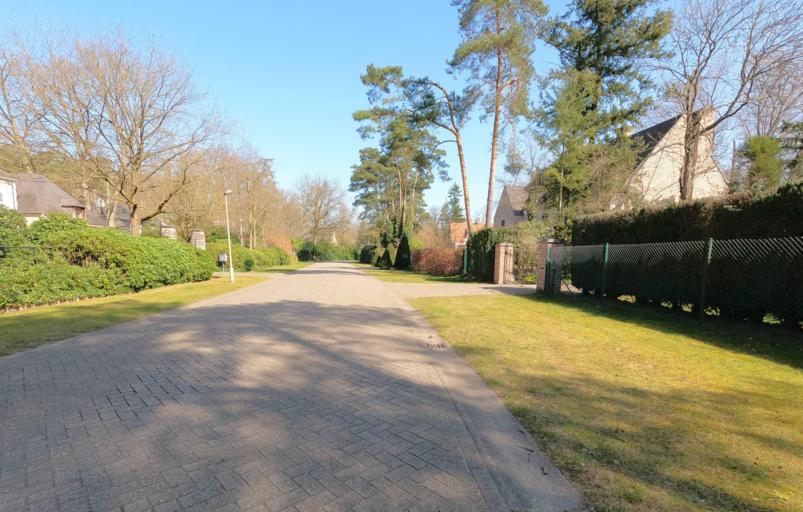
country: BE
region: Flanders
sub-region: Provincie Antwerpen
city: Schilde
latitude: 51.2478
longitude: 4.5699
